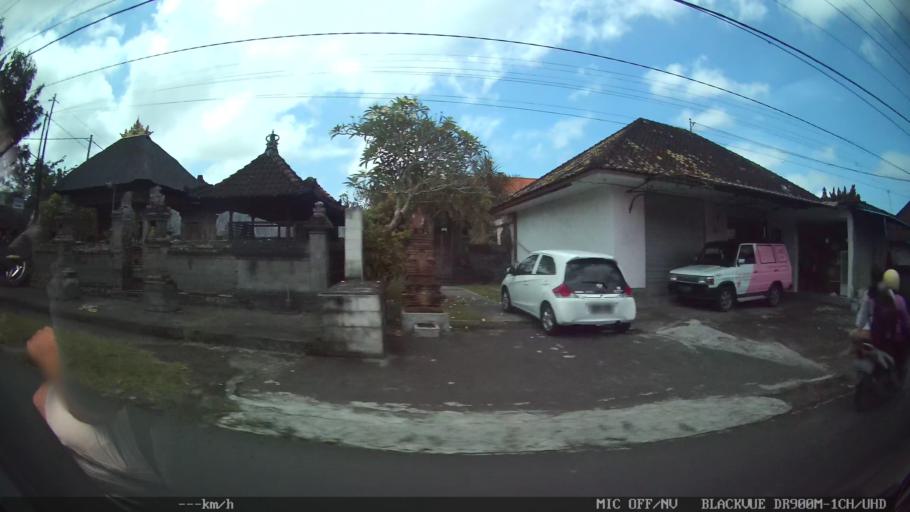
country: ID
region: Bali
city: Banjar Sedang
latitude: -8.5609
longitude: 115.2865
